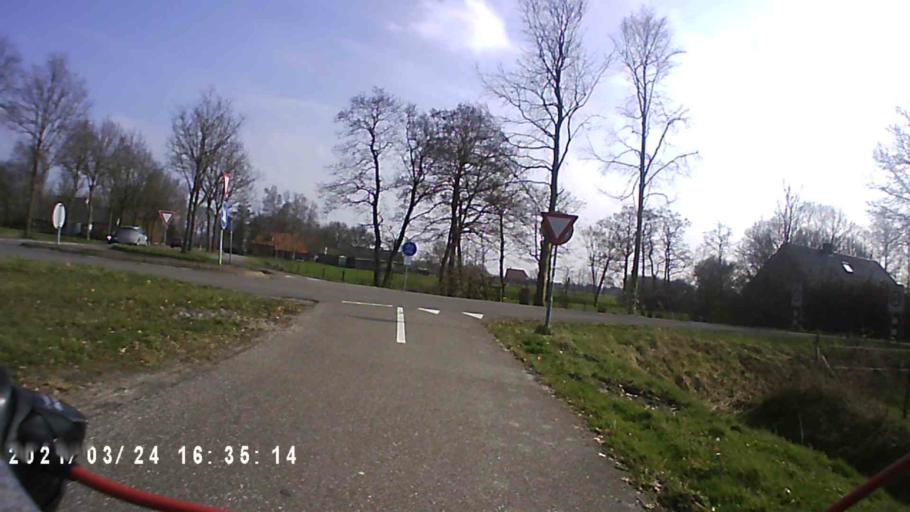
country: NL
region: Groningen
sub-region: Gemeente Leek
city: Leek
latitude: 53.0666
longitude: 6.2735
